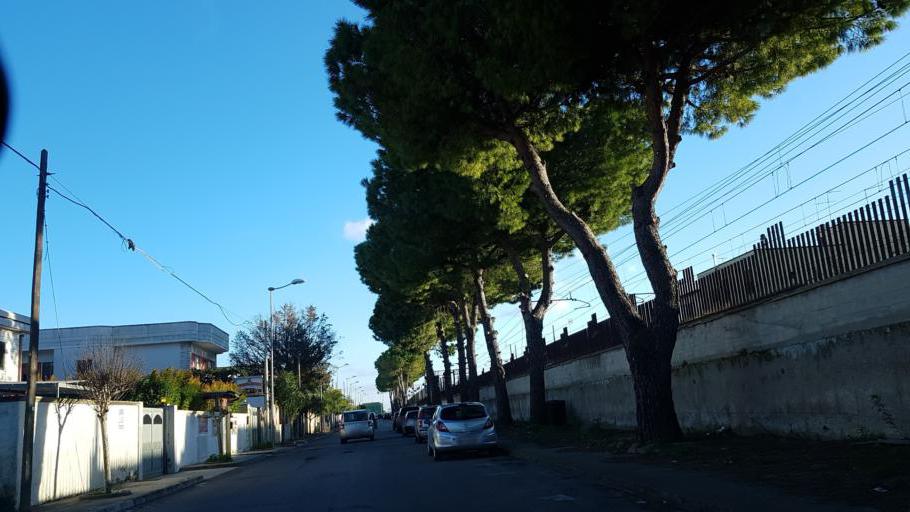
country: IT
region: Apulia
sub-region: Provincia di Lecce
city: Squinzano
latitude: 40.4361
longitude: 18.0497
